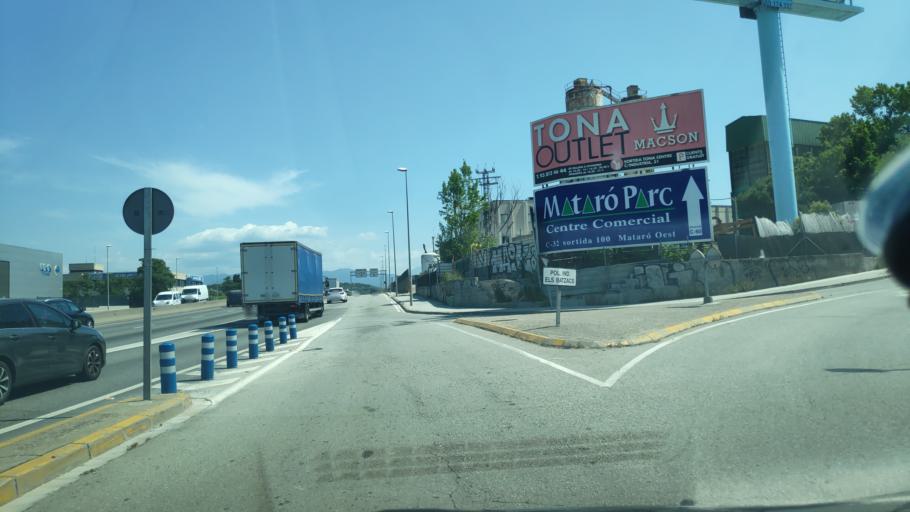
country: ES
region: Catalonia
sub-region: Provincia de Barcelona
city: Llica de Vall
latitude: 41.5845
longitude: 2.2563
